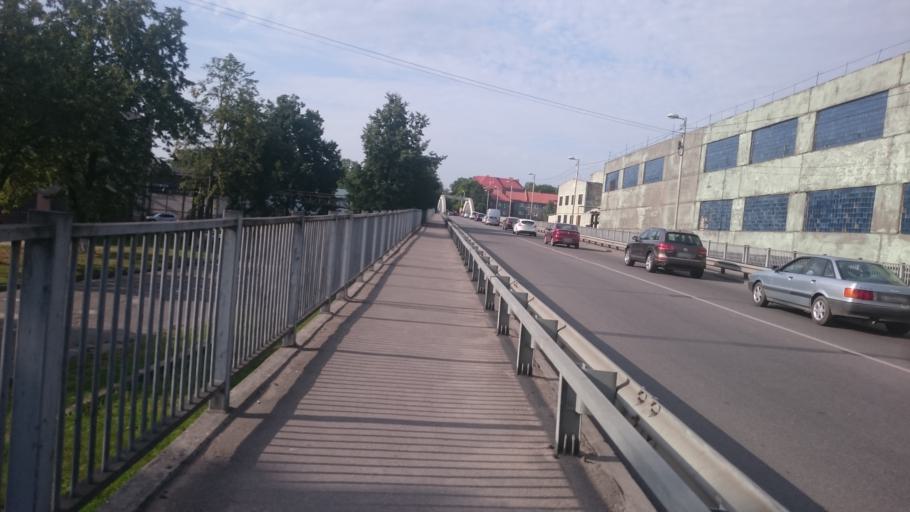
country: RU
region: Kaliningrad
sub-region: Gorod Kaliningrad
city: Kaliningrad
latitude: 54.7087
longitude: 20.4588
